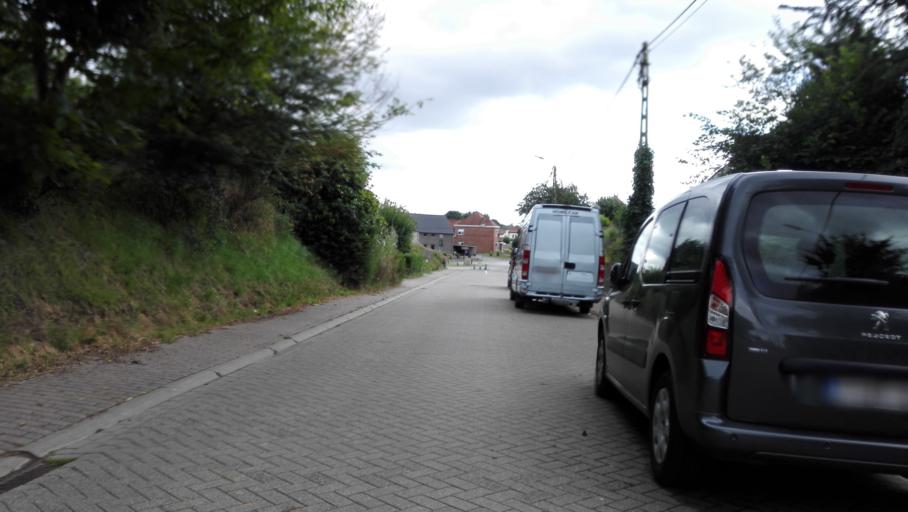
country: BE
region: Flanders
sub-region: Provincie Vlaams-Brabant
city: Bertem
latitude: 50.8625
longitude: 4.6376
